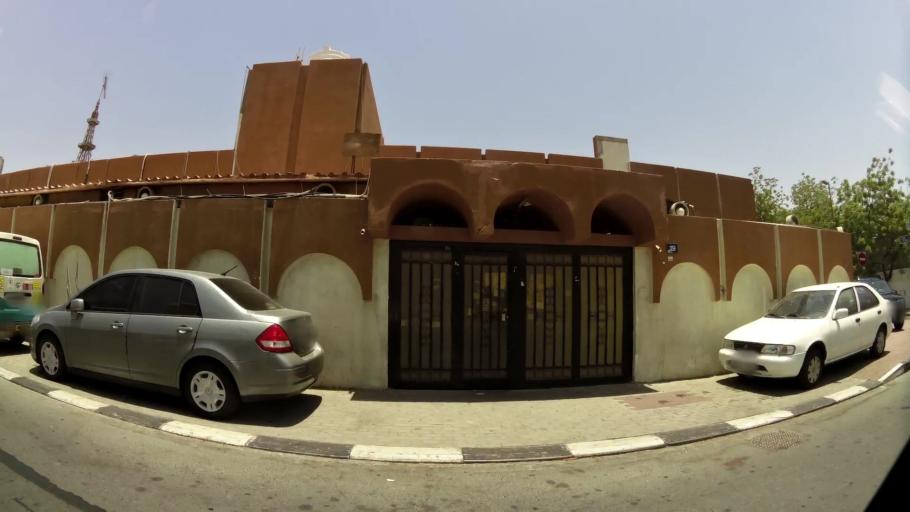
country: AE
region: Ash Shariqah
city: Sharjah
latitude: 25.2423
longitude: 55.2837
